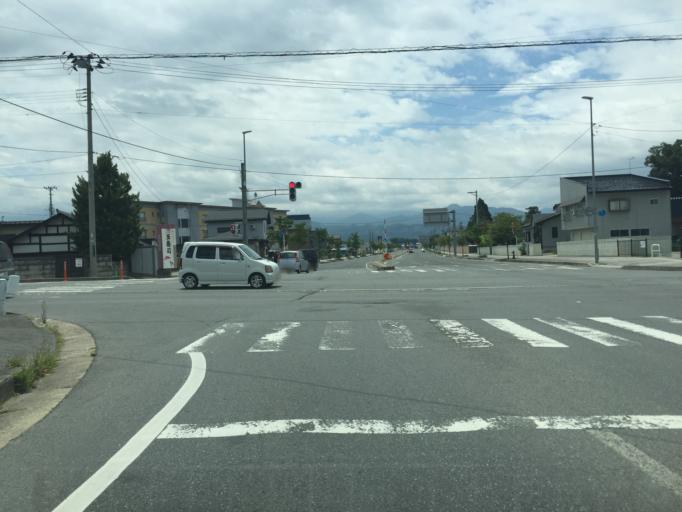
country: JP
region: Yamagata
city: Yonezawa
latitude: 37.9094
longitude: 140.1178
